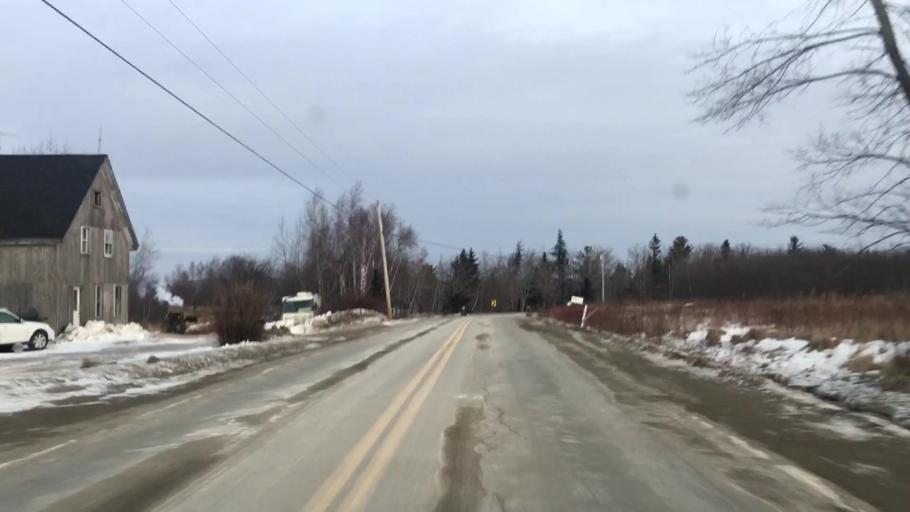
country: US
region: Maine
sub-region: Hancock County
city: Franklin
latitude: 44.7332
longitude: -68.3360
